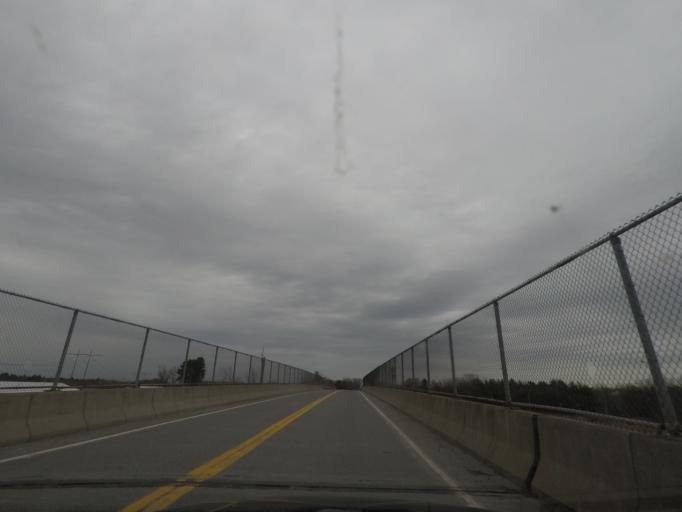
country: US
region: New York
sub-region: Rensselaer County
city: Castleton-on-Hudson
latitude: 42.5421
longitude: -73.8174
